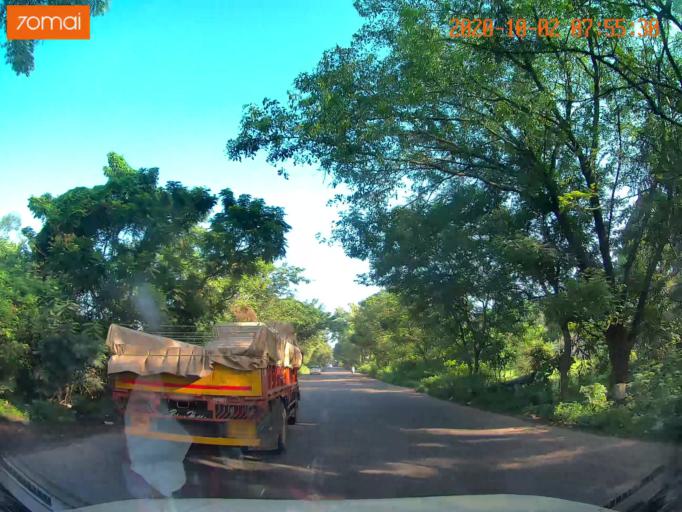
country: IN
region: Kerala
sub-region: Kozhikode
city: Ferokh
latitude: 11.1831
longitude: 75.8716
